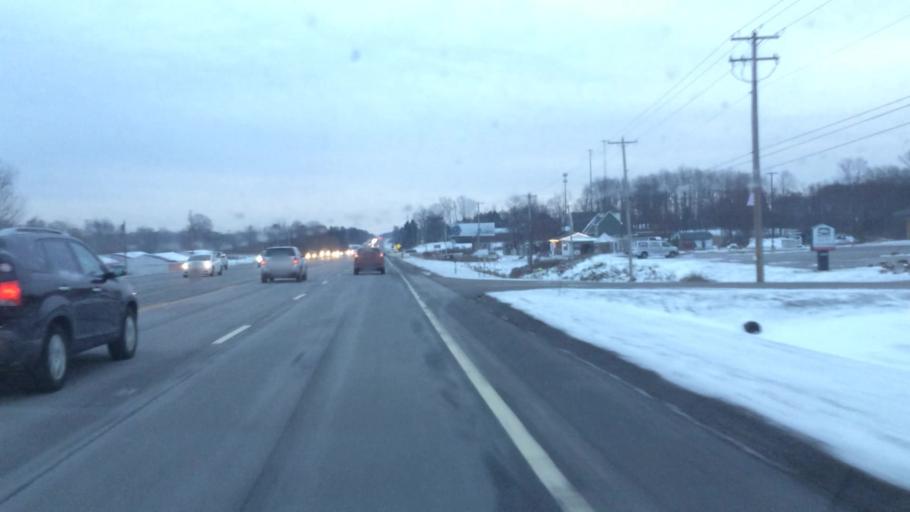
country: US
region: Ohio
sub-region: Summit County
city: Montrose-Ghent
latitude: 41.1362
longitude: -81.7116
